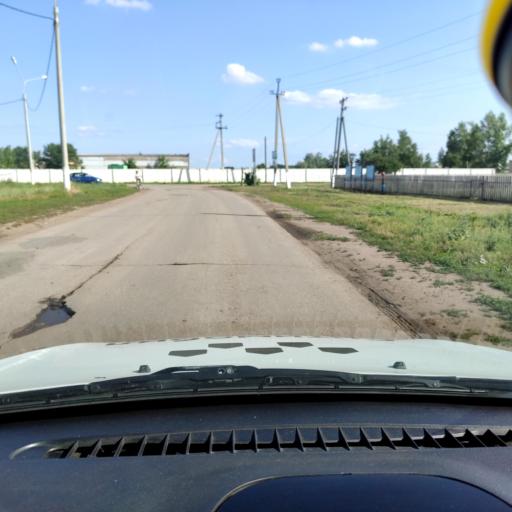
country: RU
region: Samara
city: Tol'yatti
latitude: 53.3524
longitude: 49.2974
